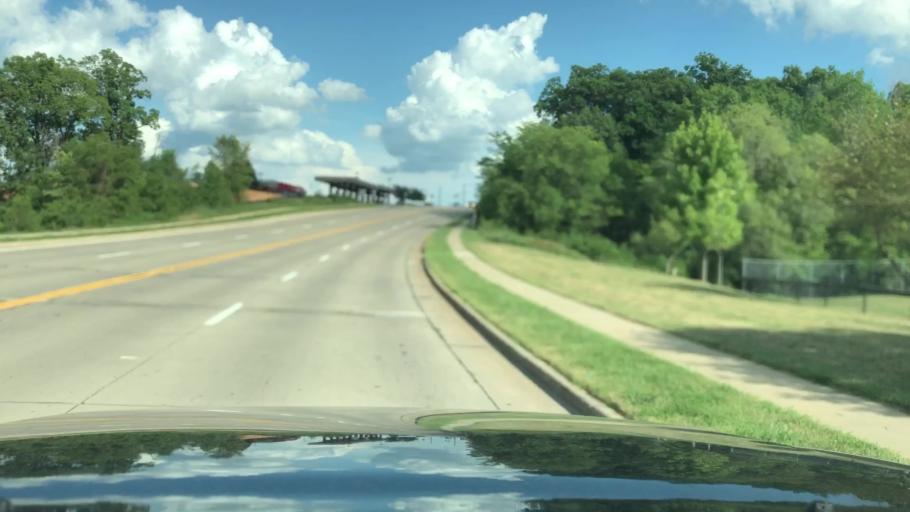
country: US
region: Missouri
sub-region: Saint Charles County
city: Wentzville
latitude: 38.8242
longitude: -90.8555
